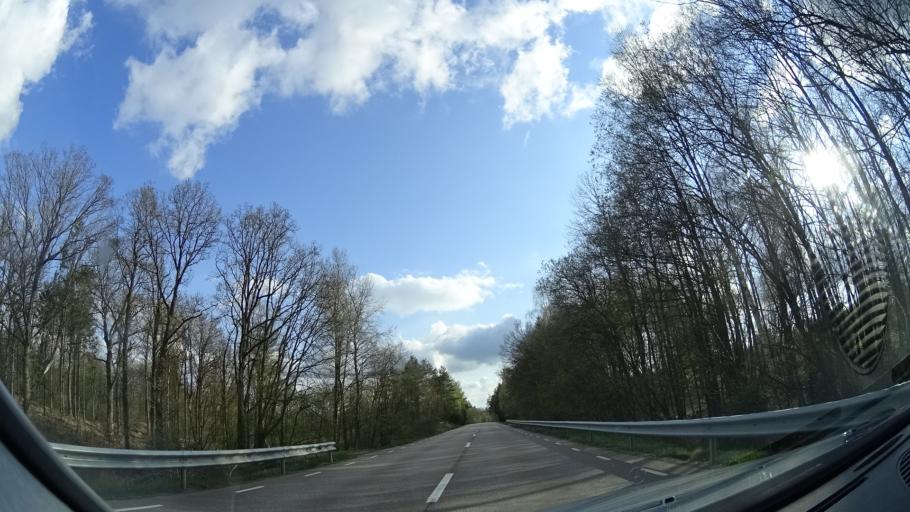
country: SE
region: Skane
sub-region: Perstorps Kommun
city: Perstorp
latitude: 56.1232
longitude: 13.3020
